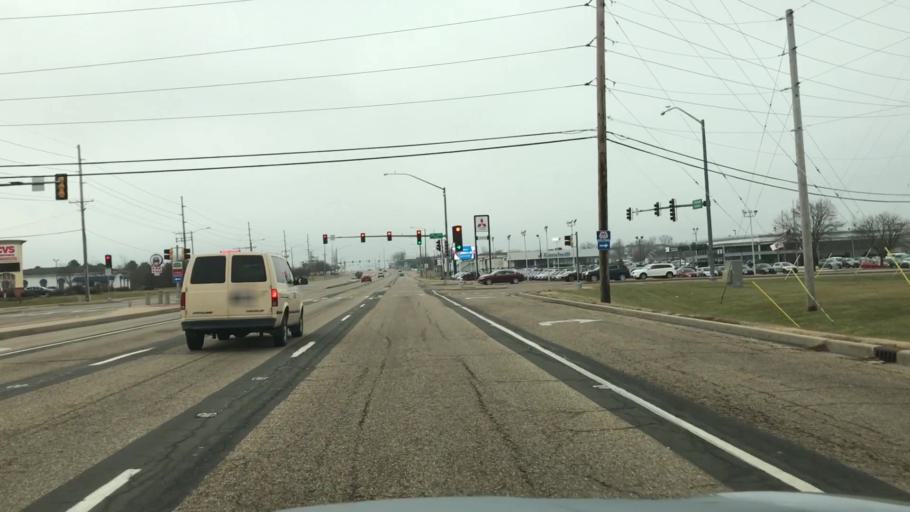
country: US
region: Illinois
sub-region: McLean County
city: Normal
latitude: 40.5184
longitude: -88.9530
